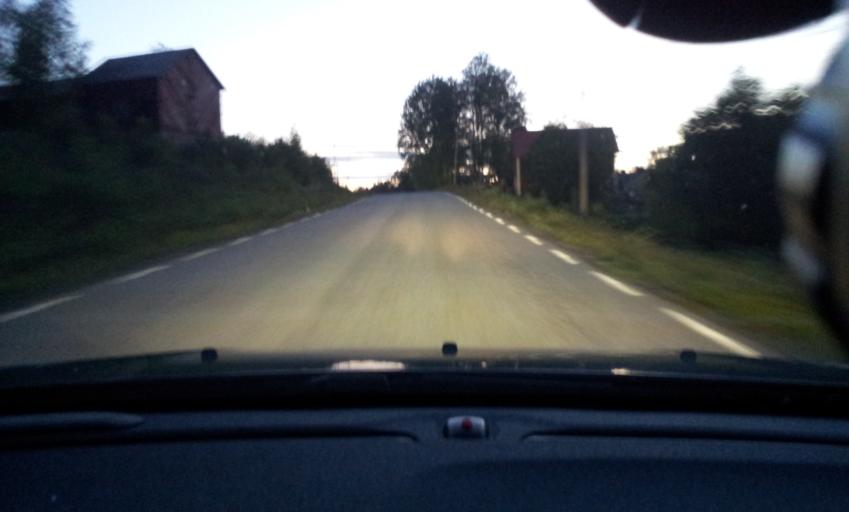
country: SE
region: Jaemtland
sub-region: Bergs Kommun
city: Hoverberg
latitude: 62.7608
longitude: 14.5614
